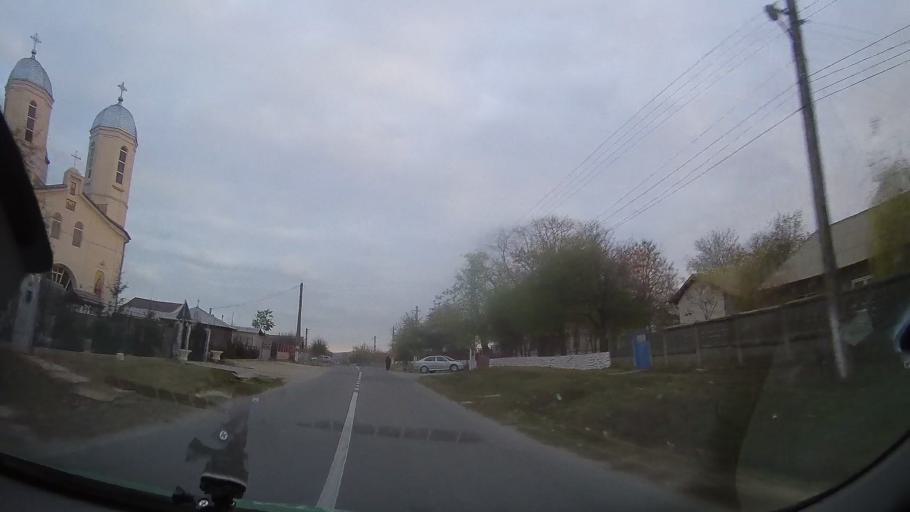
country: RO
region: Tulcea
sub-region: Comuna Mihai Bravu
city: Turda
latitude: 44.9763
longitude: 28.6206
